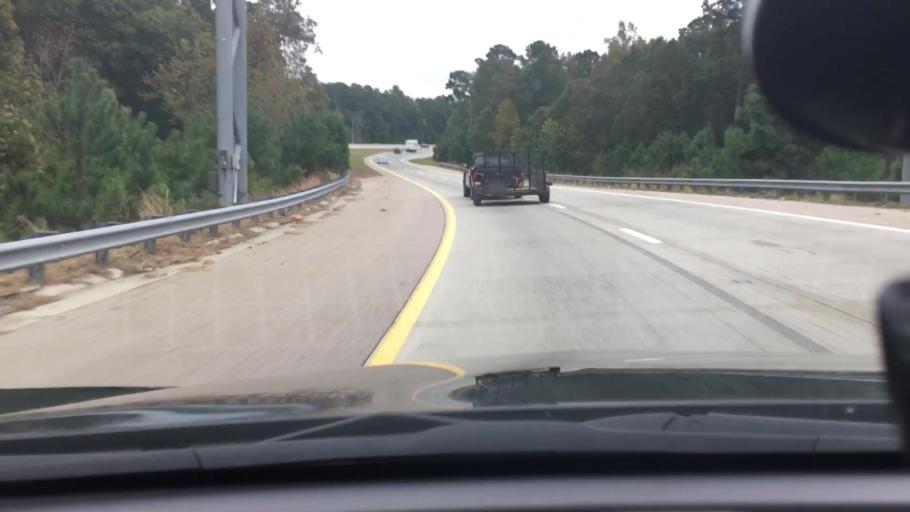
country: US
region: North Carolina
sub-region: Wake County
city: Raleigh
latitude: 35.7785
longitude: -78.5755
